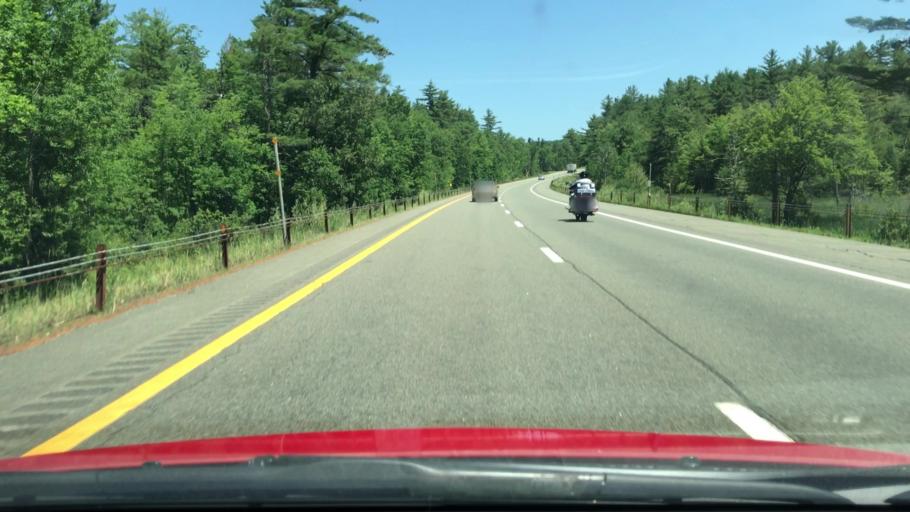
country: US
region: New York
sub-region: Essex County
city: Keeseville
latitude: 44.3729
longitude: -73.5253
